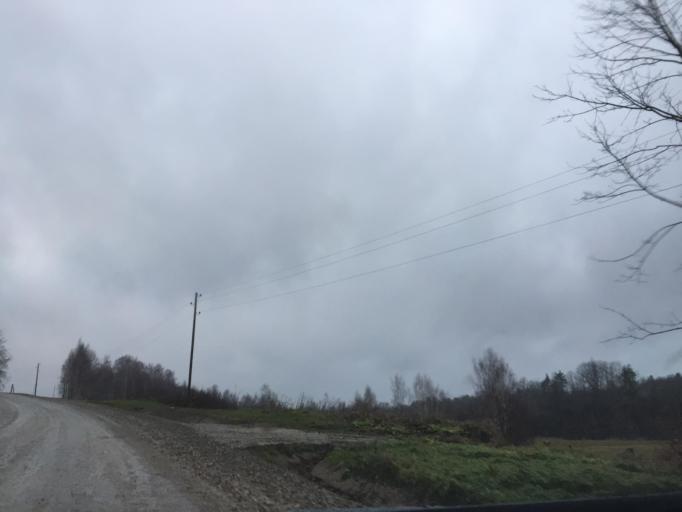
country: LV
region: Salacgrivas
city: Salacgriva
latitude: 57.7584
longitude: 24.4541
